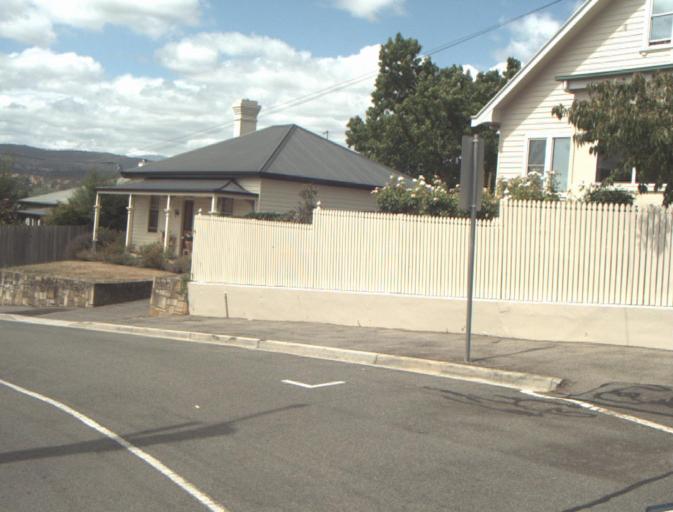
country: AU
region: Tasmania
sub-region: Launceston
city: East Launceston
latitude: -41.4369
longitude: 147.1524
